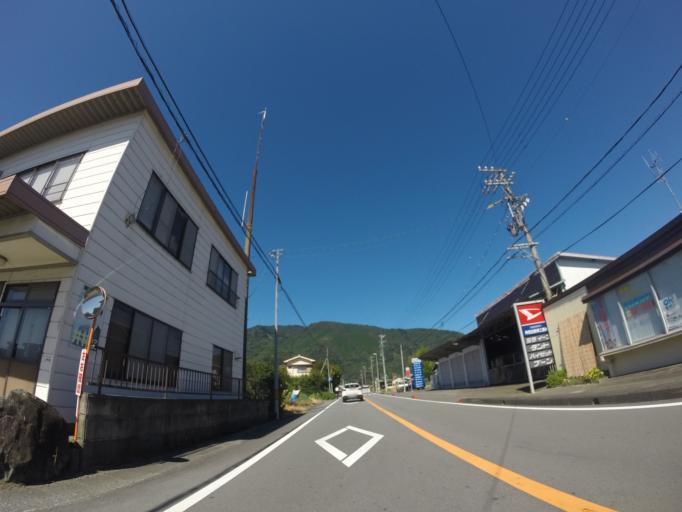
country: JP
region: Shizuoka
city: Kanaya
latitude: 34.8738
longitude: 138.1113
